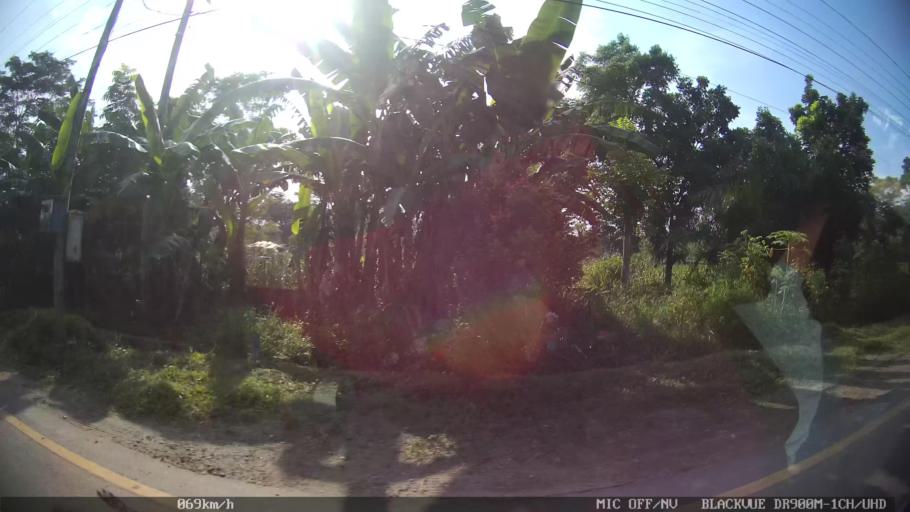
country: ID
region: North Sumatra
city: Percut
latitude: 3.5882
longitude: 98.8045
